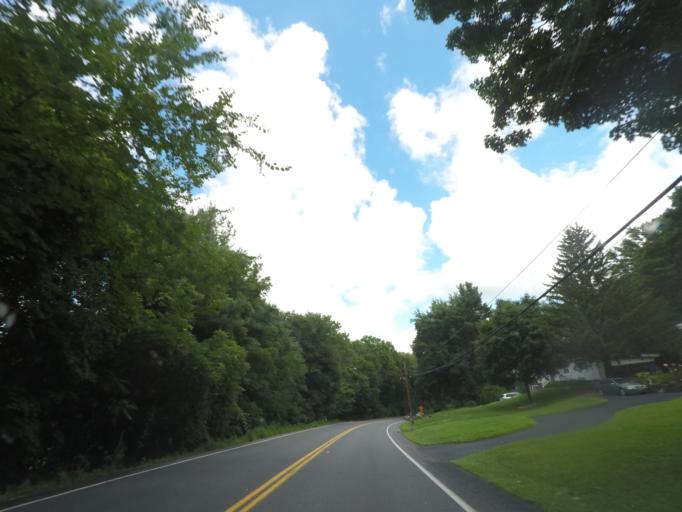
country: US
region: New York
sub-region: Rensselaer County
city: Wynantskill
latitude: 42.6953
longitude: -73.6669
